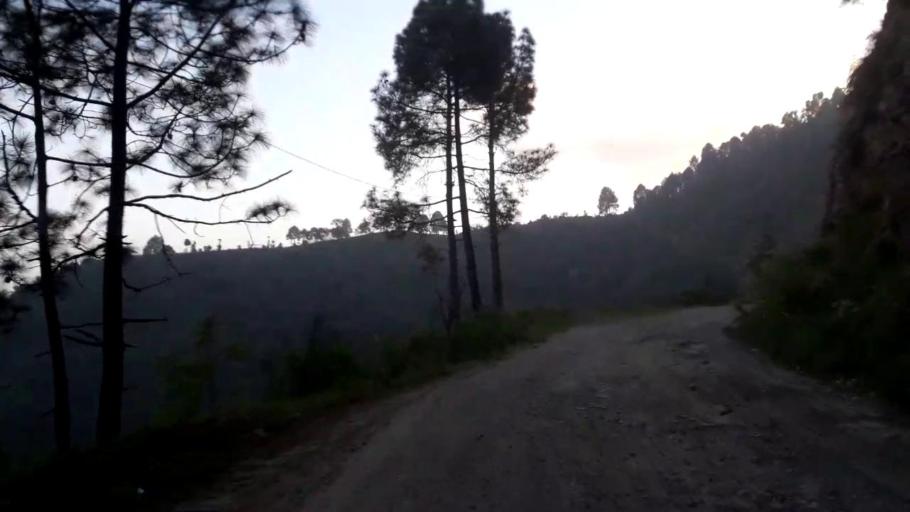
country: IN
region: Himachal Pradesh
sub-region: Shimla
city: Shimla
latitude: 31.0565
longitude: 77.1569
